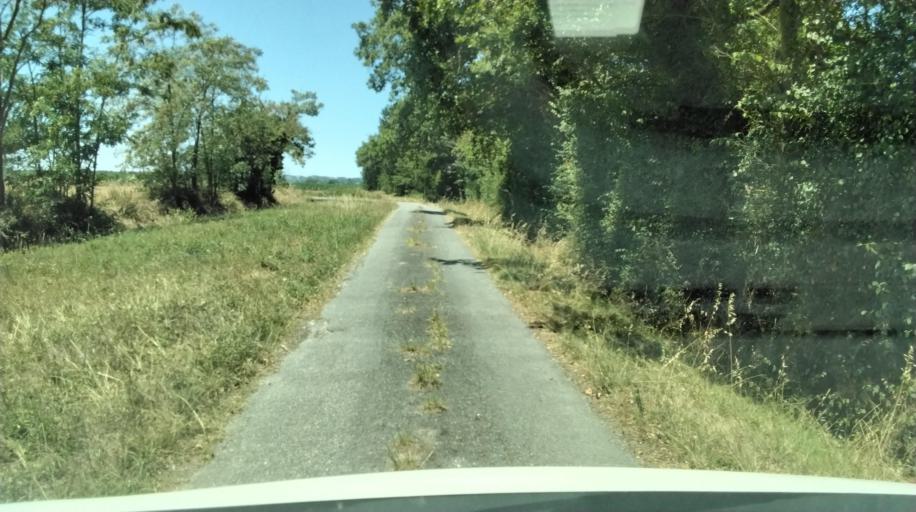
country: FR
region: Midi-Pyrenees
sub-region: Departement de la Haute-Garonne
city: Le Fousseret
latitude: 43.2757
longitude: 1.1292
